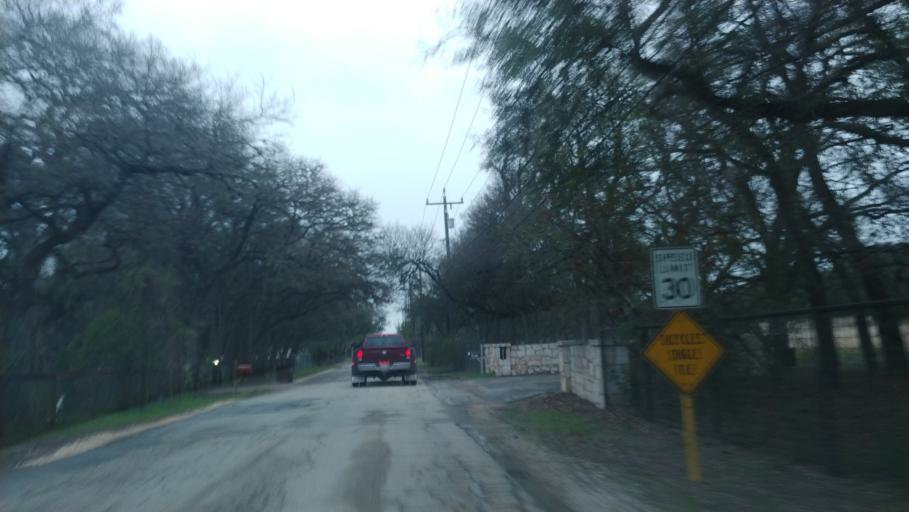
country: US
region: Texas
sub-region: Bexar County
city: Cross Mountain
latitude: 29.6177
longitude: -98.6852
